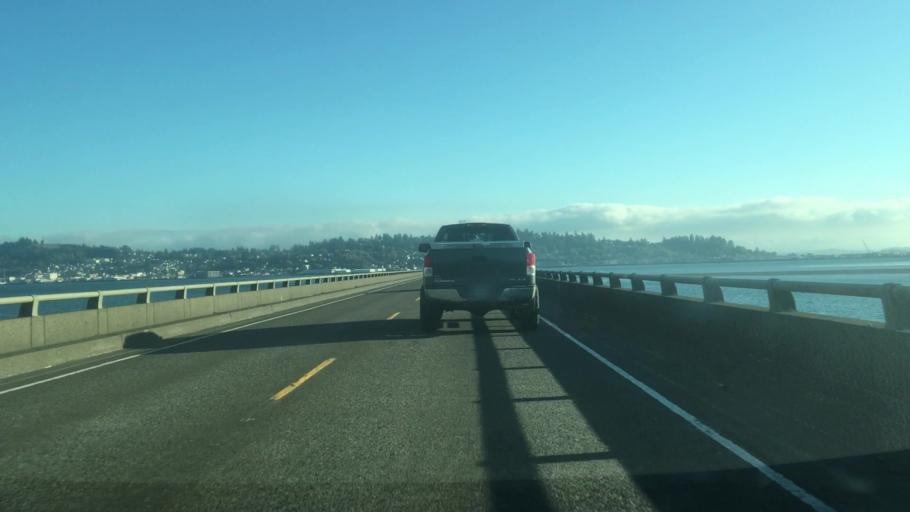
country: US
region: Oregon
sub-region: Clatsop County
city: Astoria
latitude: 46.2117
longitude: -123.8601
